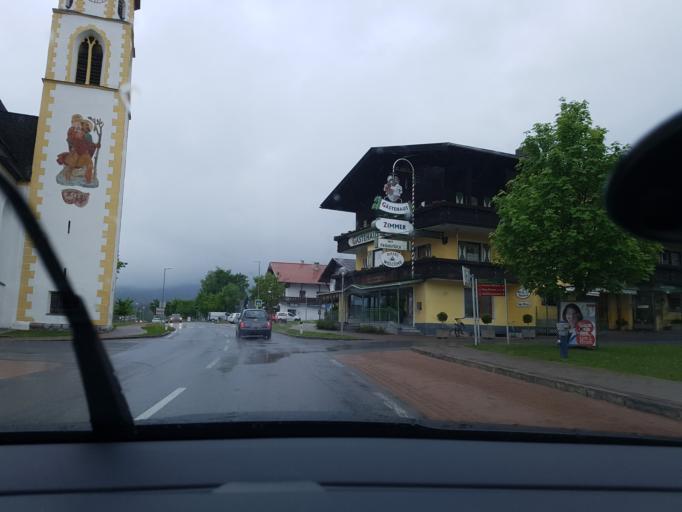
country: AT
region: Tyrol
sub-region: Politischer Bezirk Imst
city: Mieming
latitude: 47.3048
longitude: 10.9678
